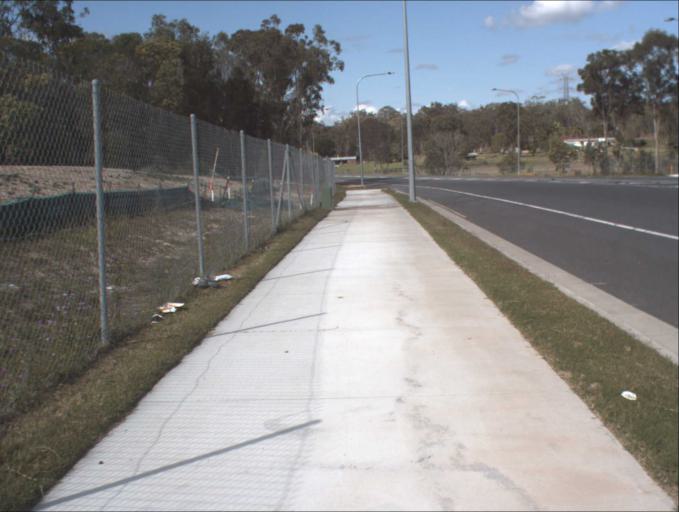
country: AU
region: Queensland
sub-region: Logan
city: Logan Reserve
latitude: -27.6890
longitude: 153.0696
